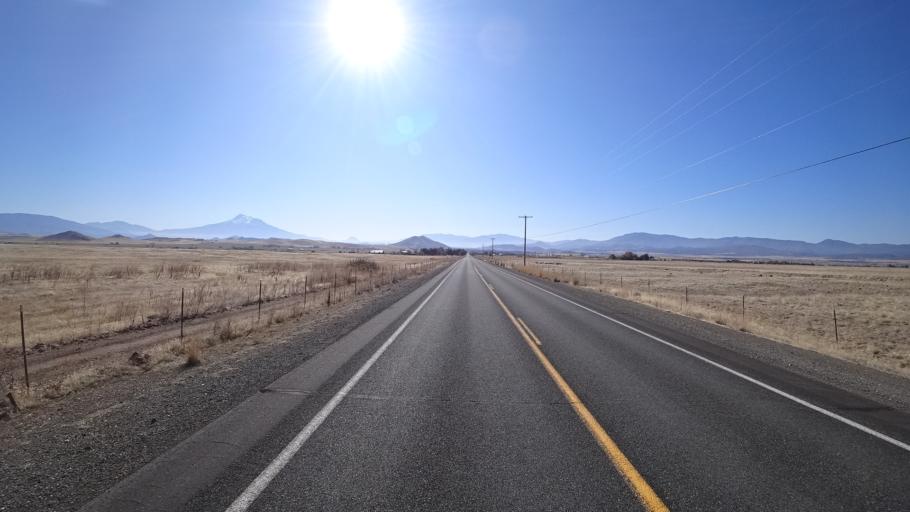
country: US
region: California
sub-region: Siskiyou County
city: Montague
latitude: 41.7693
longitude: -122.5246
